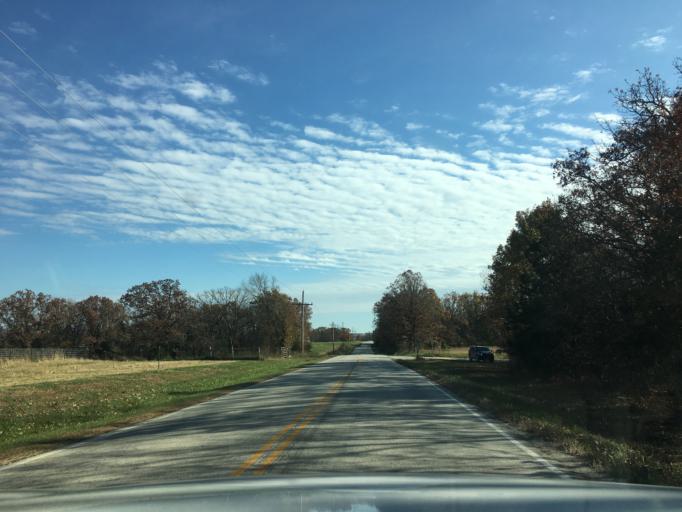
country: US
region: Missouri
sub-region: Maries County
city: Belle
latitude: 38.3584
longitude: -91.8049
